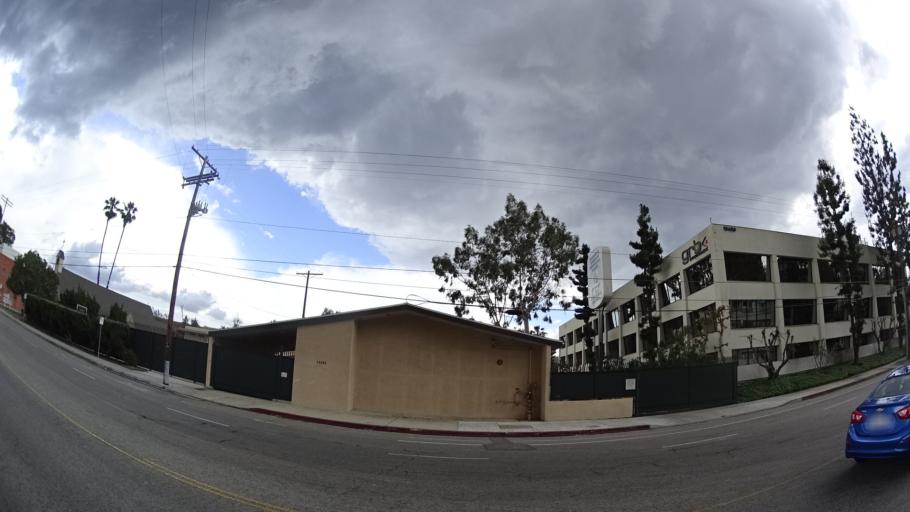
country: US
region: California
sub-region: Los Angeles County
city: Sherman Oaks
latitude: 34.1577
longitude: -118.4243
